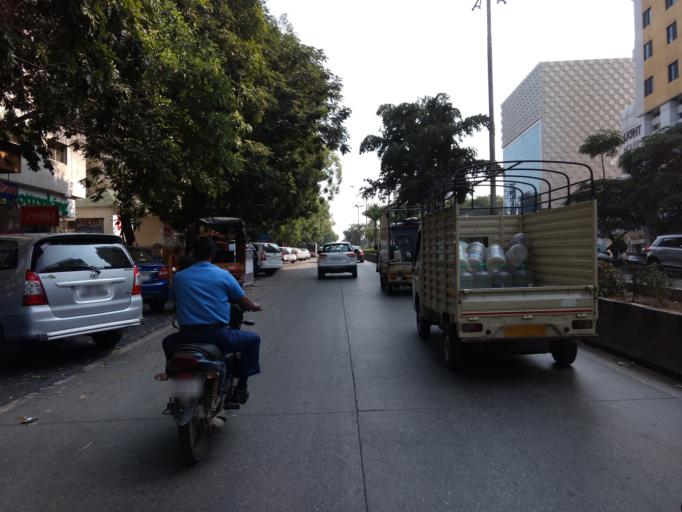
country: IN
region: Maharashtra
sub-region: Pune Division
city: Pune
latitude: 18.4809
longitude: 73.8624
